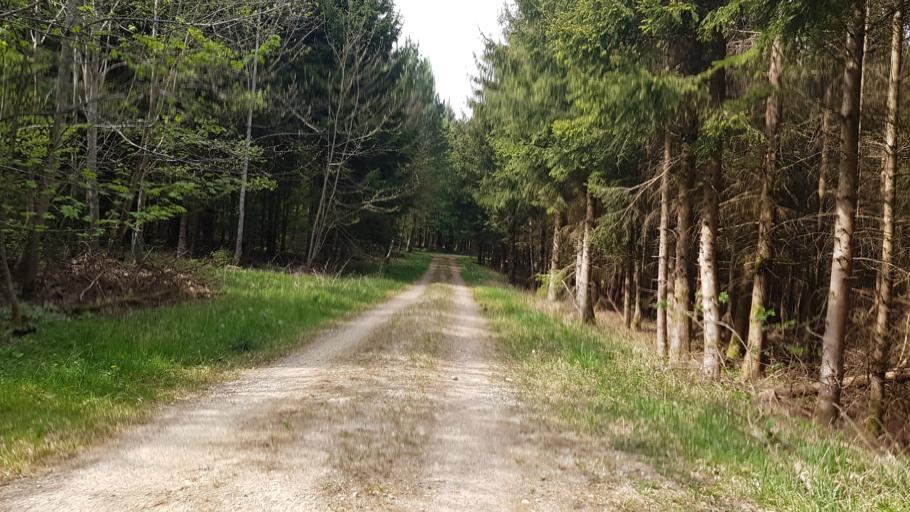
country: CH
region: Aargau
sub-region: Bezirk Kulm
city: Reinach
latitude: 47.2836
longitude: 8.1819
